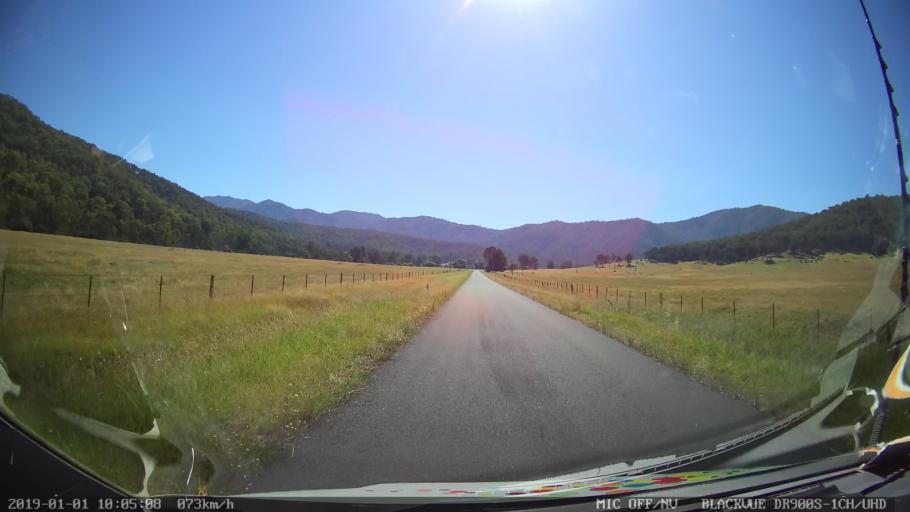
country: AU
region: New South Wales
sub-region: Snowy River
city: Jindabyne
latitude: -36.1743
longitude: 148.1318
